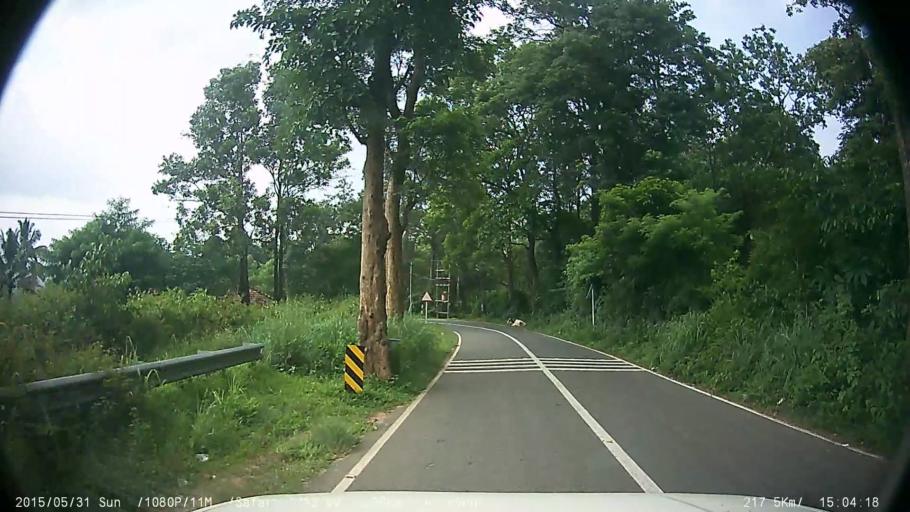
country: IN
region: Kerala
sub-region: Wayanad
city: Kalpetta
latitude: 11.6350
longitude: 76.2139
